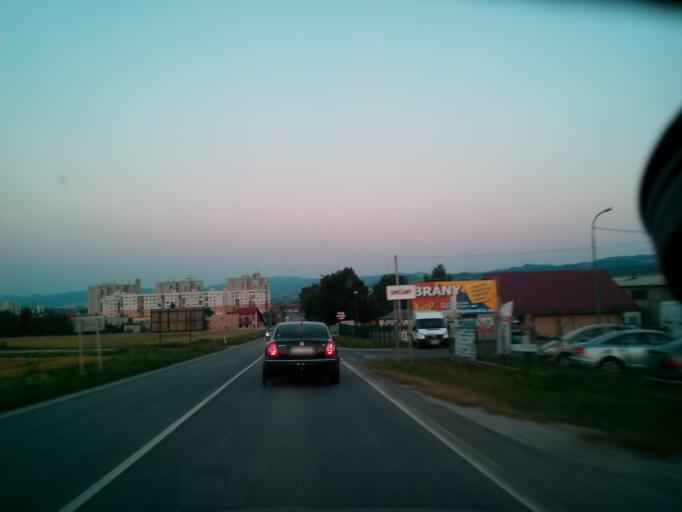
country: SK
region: Kosicky
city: Spisska Nova Ves
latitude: 48.9595
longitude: 20.5079
